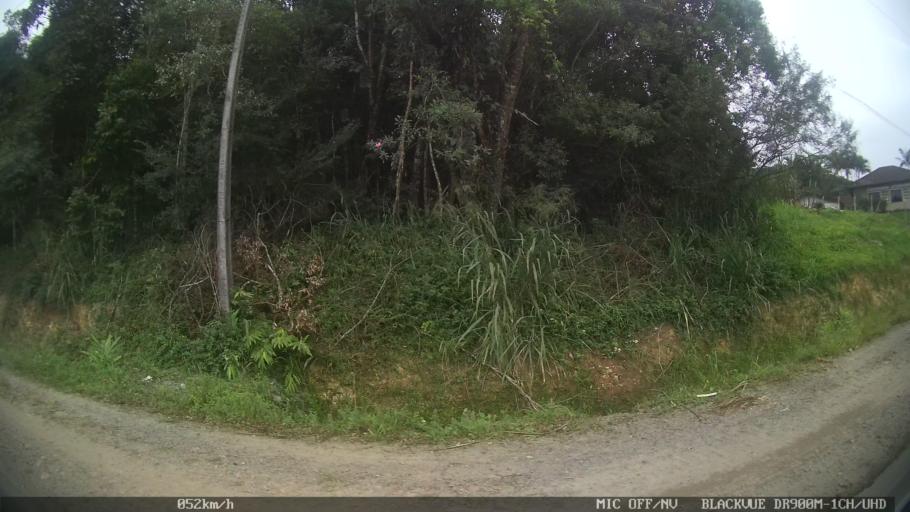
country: BR
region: Santa Catarina
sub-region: Joinville
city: Joinville
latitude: -26.2173
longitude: -48.9045
